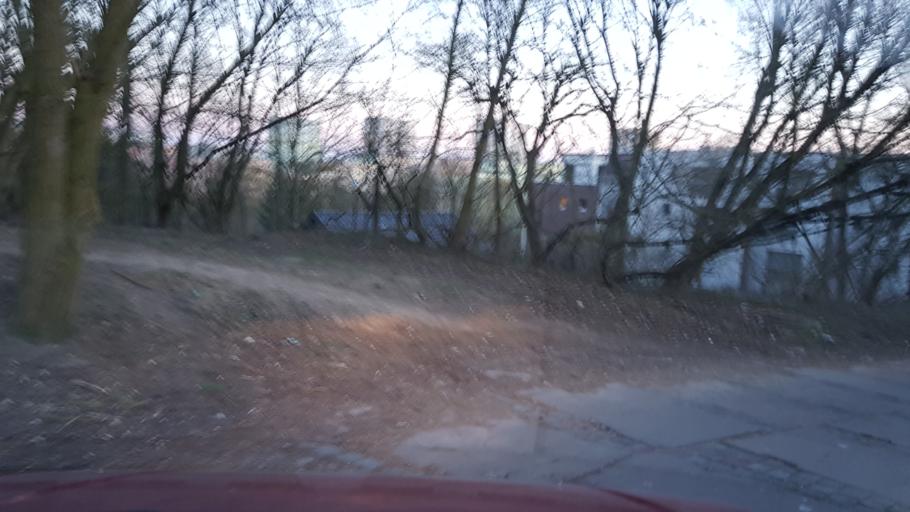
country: PL
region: West Pomeranian Voivodeship
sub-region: Szczecin
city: Szczecin
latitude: 53.4620
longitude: 14.5347
